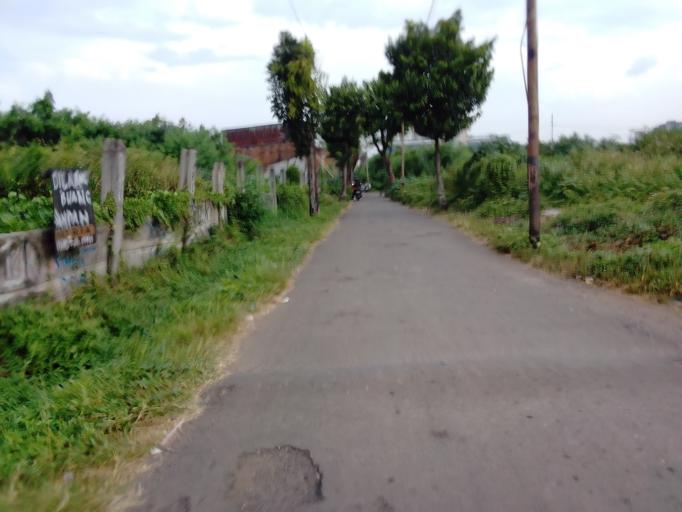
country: ID
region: Jakarta Raya
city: Jakarta
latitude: -6.1624
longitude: 106.8034
